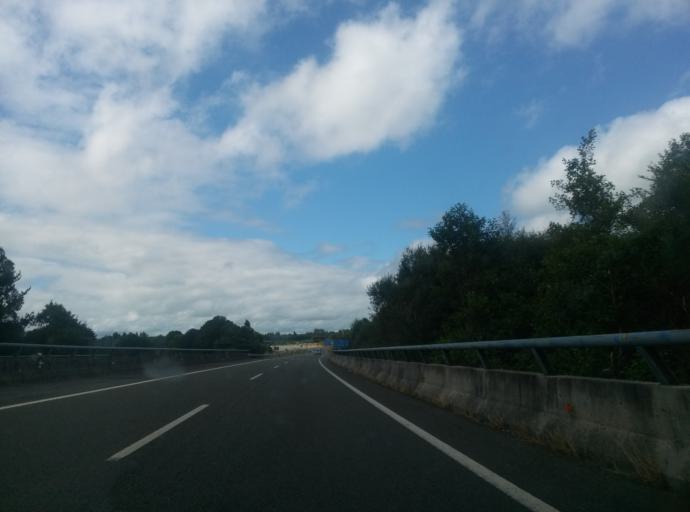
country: ES
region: Galicia
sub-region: Provincia de Lugo
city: Rabade
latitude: 43.1208
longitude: -7.6113
